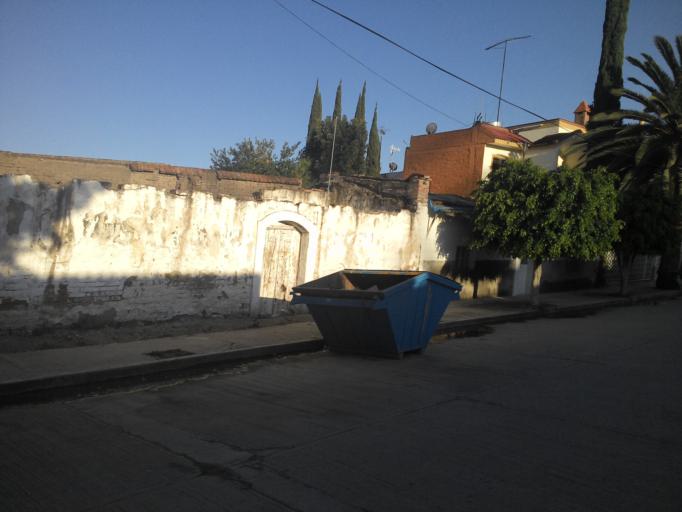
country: MX
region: Jalisco
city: San Diego de Alejandria
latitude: 20.8802
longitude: -101.9842
